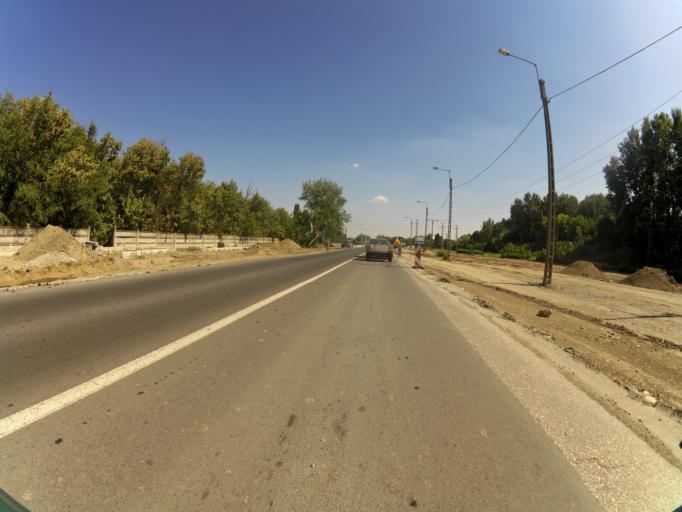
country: HU
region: Csongrad
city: Szeged
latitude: 46.2759
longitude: 20.0990
